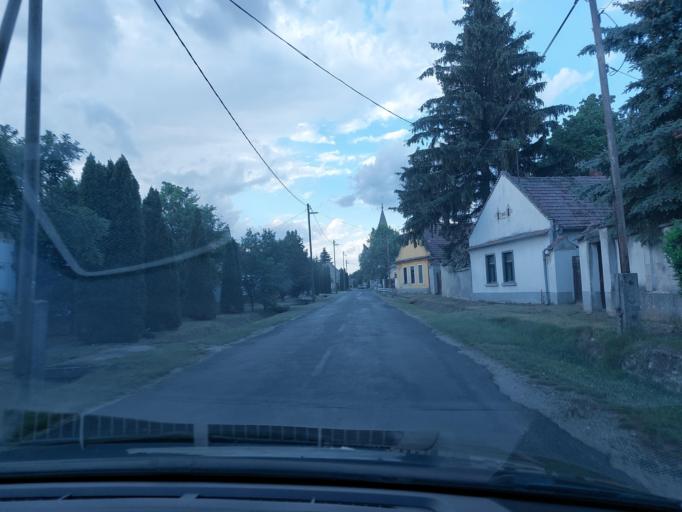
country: HU
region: Veszprem
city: Devecser
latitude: 47.1936
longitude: 17.3517
